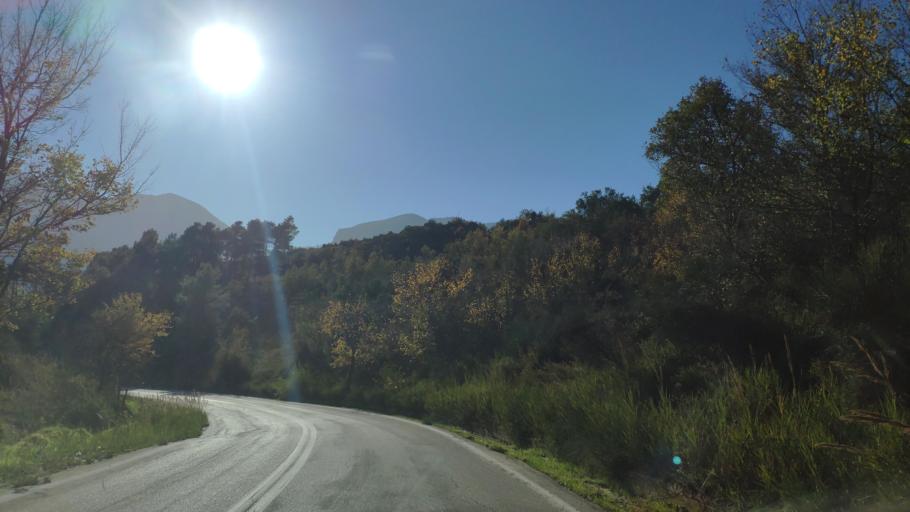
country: GR
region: Peloponnese
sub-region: Nomos Korinthias
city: Xylokastro
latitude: 38.0033
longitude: 22.5046
